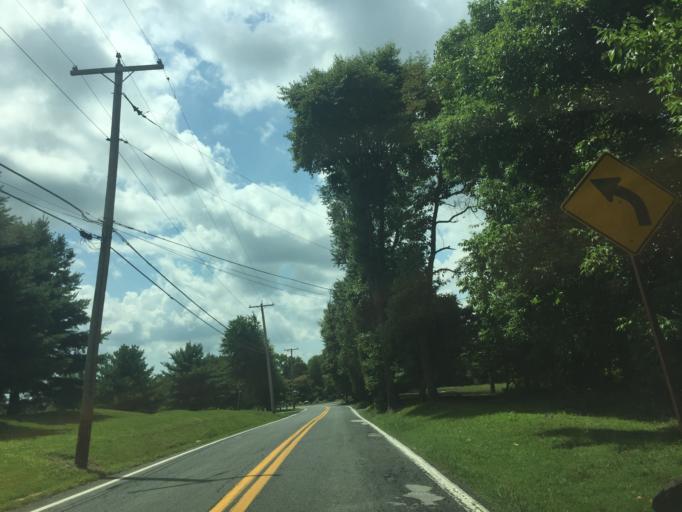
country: US
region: Maryland
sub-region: Baltimore County
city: Kingsville
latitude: 39.4242
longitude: -76.4076
